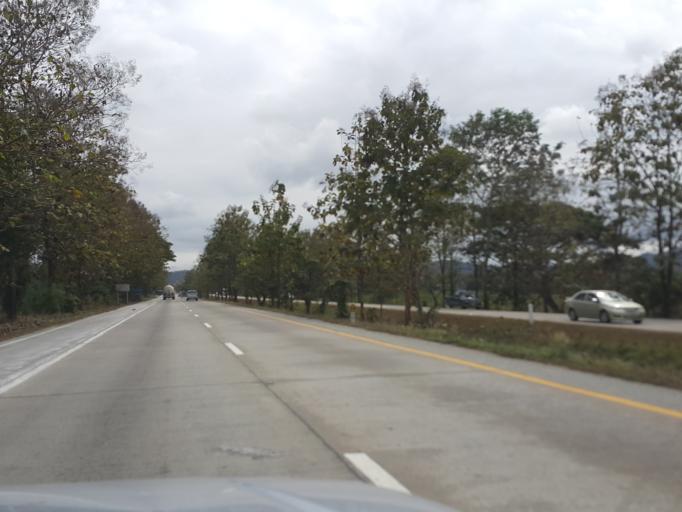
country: TH
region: Lamphun
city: Mae Tha
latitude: 18.5271
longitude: 99.0822
